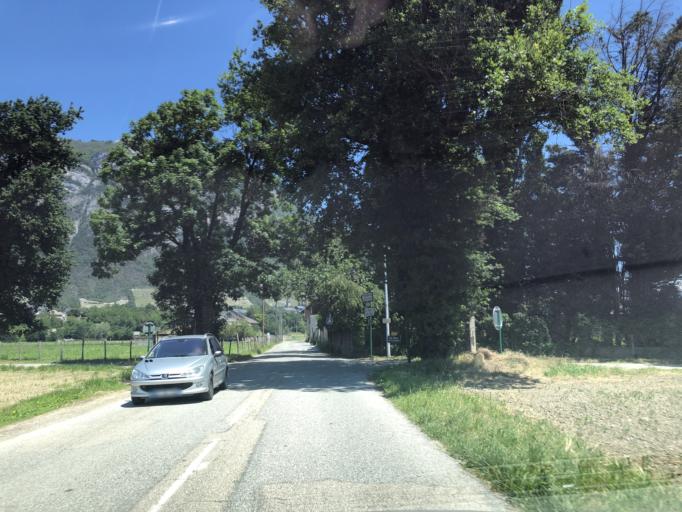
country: FR
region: Rhone-Alpes
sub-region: Departement de la Savoie
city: Montmelian
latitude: 45.4931
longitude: 6.0278
